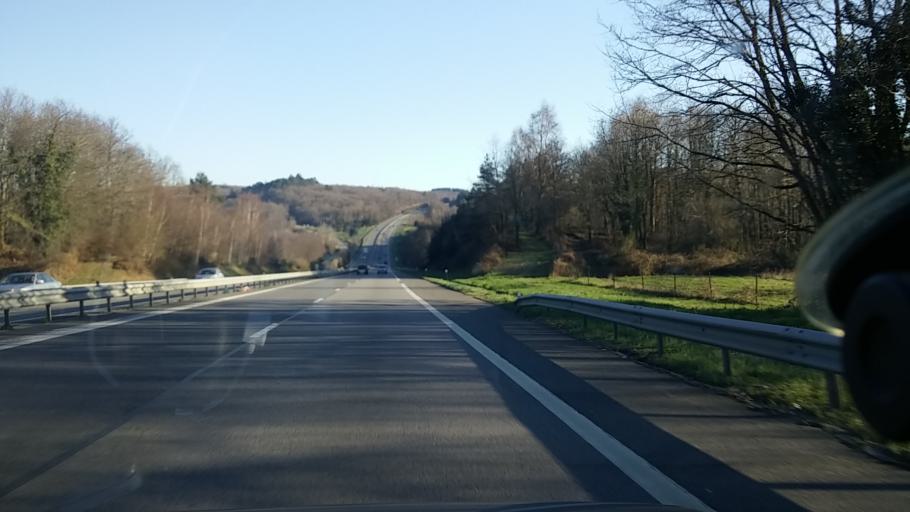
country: FR
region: Limousin
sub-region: Departement de la Haute-Vienne
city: Bessines-sur-Gartempe
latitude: 46.0770
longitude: 1.3579
